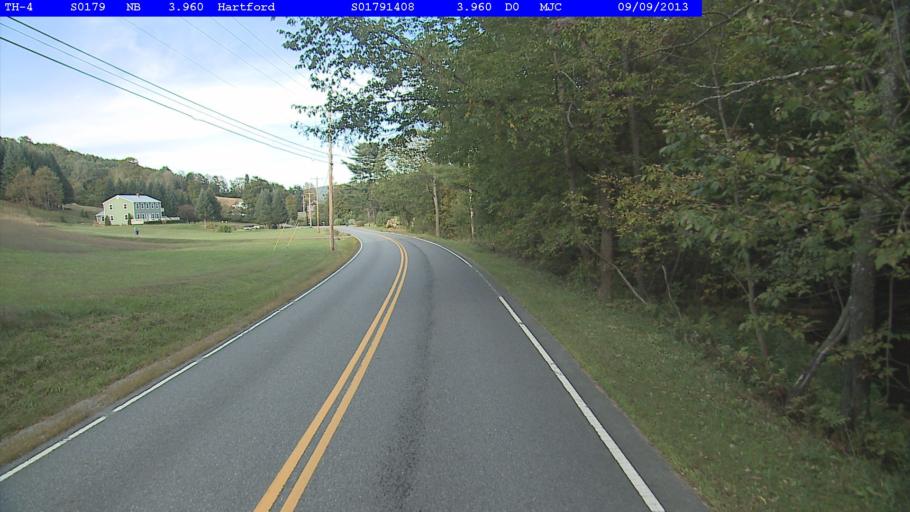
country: US
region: Vermont
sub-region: Windsor County
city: Woodstock
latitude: 43.6940
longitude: -72.4353
